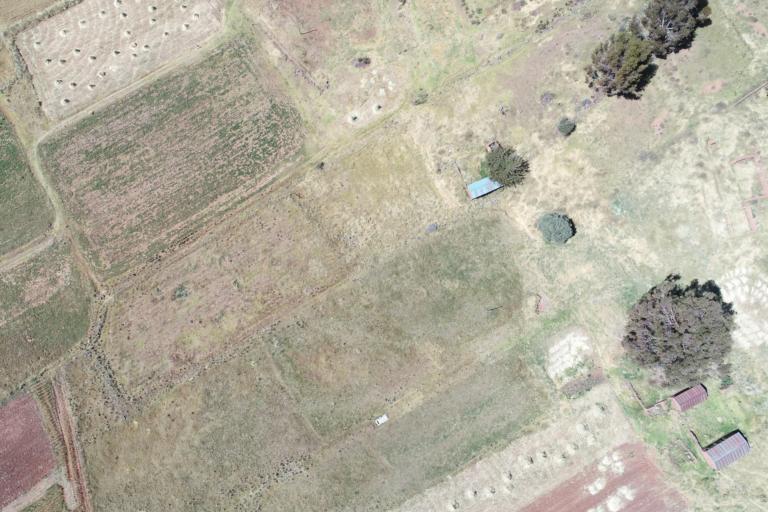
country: BO
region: La Paz
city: Tiahuanaco
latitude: -16.6026
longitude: -68.7748
